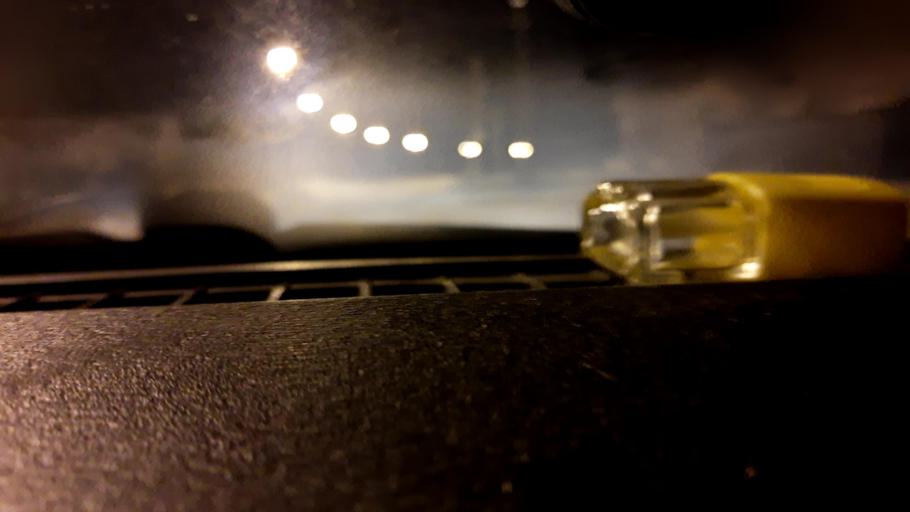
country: RU
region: Bashkortostan
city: Kabakovo
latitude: 54.6192
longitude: 56.0695
